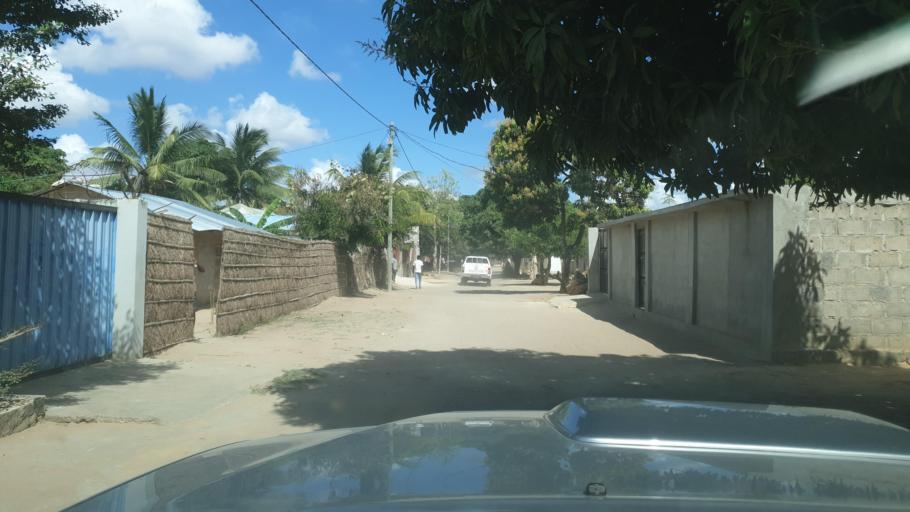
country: MZ
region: Nampula
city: Nacala
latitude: -14.5694
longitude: 40.6995
